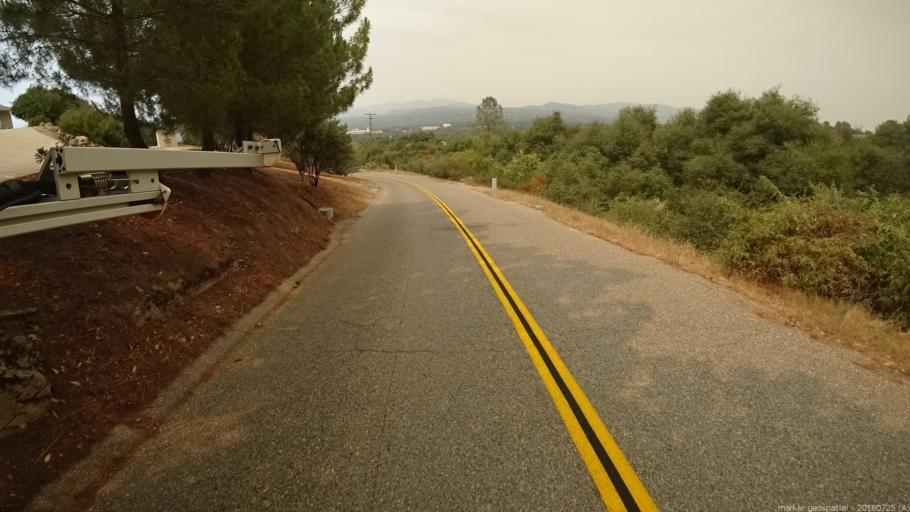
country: US
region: California
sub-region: Madera County
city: Coarsegold
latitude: 37.2013
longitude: -119.6965
